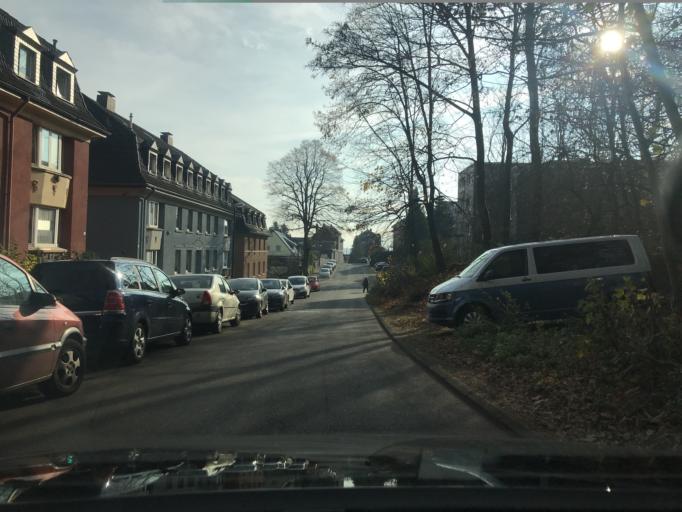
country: DE
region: North Rhine-Westphalia
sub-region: Regierungsbezirk Dusseldorf
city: Remscheid
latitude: 51.2093
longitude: 7.1410
